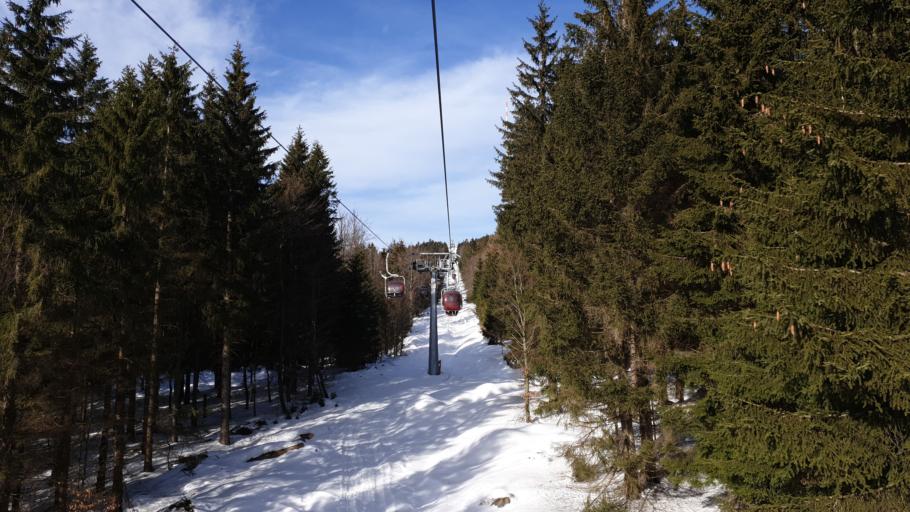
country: DE
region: Bavaria
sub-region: Upper Franconia
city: Bischofsgrun
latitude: 50.0220
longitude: 11.8081
